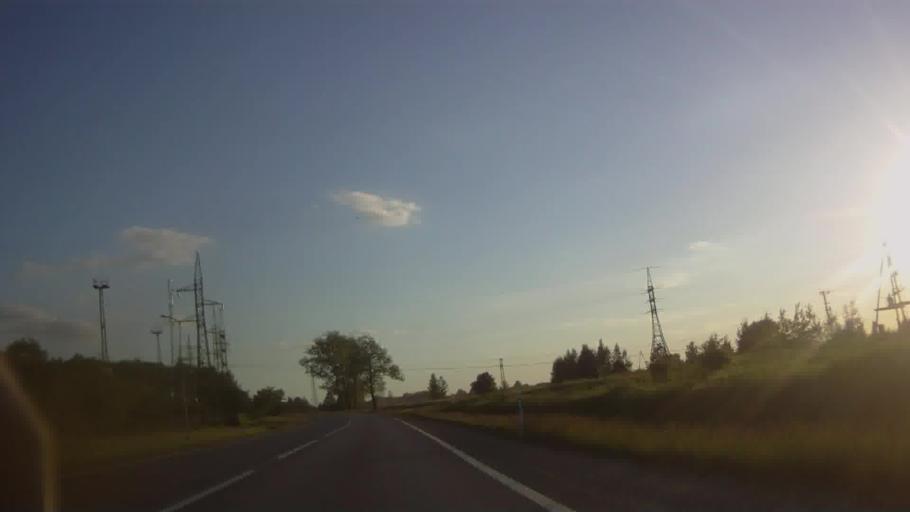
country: LV
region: Jekabpils Rajons
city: Jekabpils
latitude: 56.5245
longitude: 25.9698
